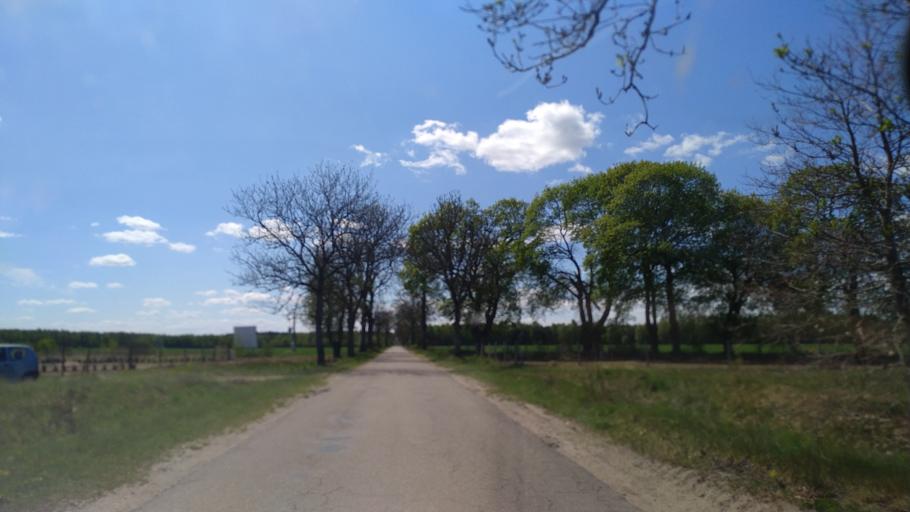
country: PL
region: Greater Poland Voivodeship
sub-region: Powiat zlotowski
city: Tarnowka
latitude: 53.2715
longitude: 16.8035
